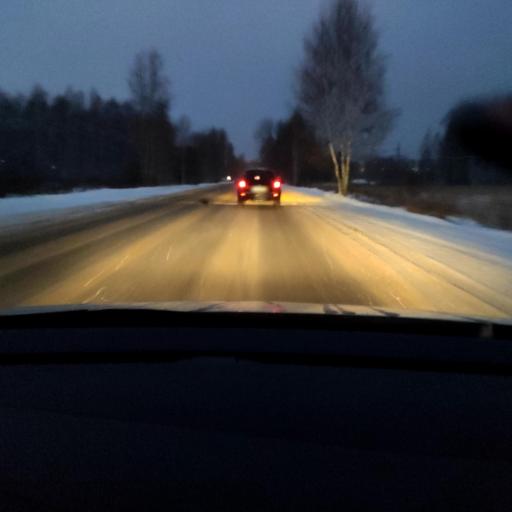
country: RU
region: Tatarstan
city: Aysha
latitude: 55.8686
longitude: 48.5807
